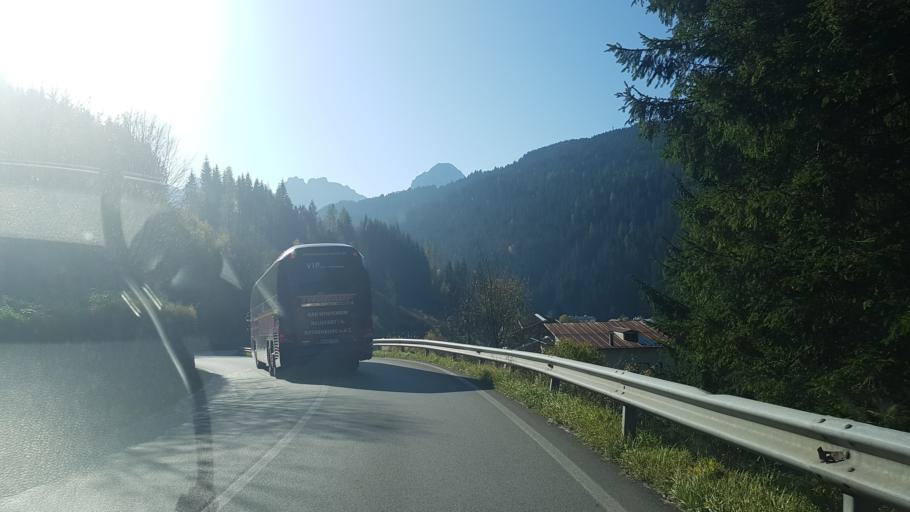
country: IT
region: Veneto
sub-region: Provincia di Belluno
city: San Nicolo Comelico
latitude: 46.5881
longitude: 12.5237
